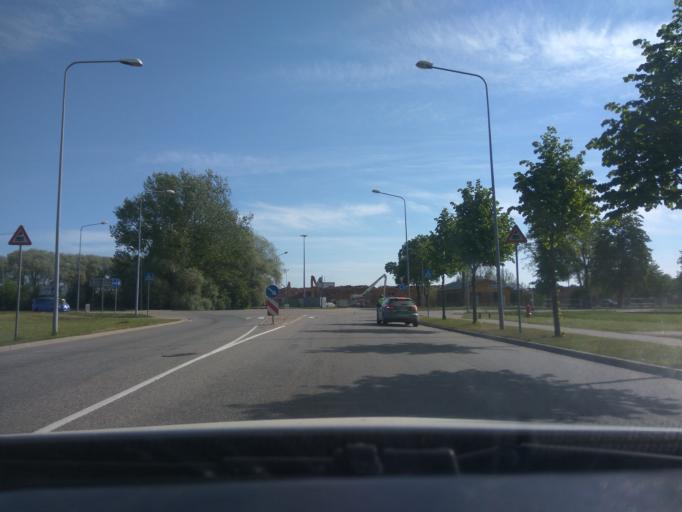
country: LV
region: Ventspils
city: Ventspils
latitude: 57.3844
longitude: 21.5864
